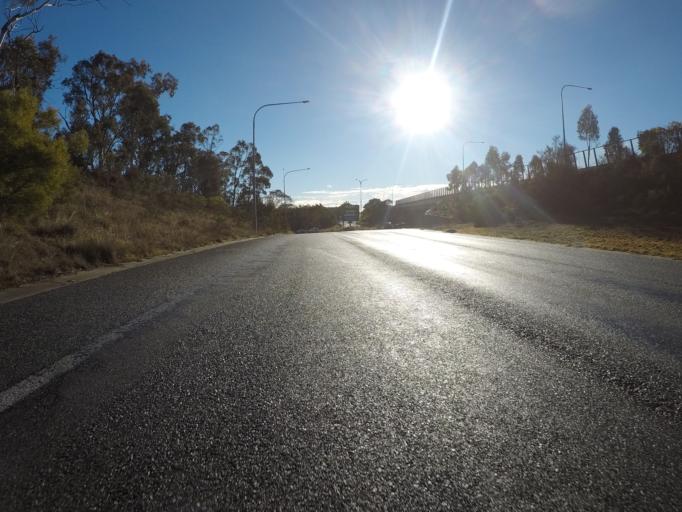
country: AU
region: Australian Capital Territory
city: Macquarie
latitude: -35.2578
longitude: 149.0882
